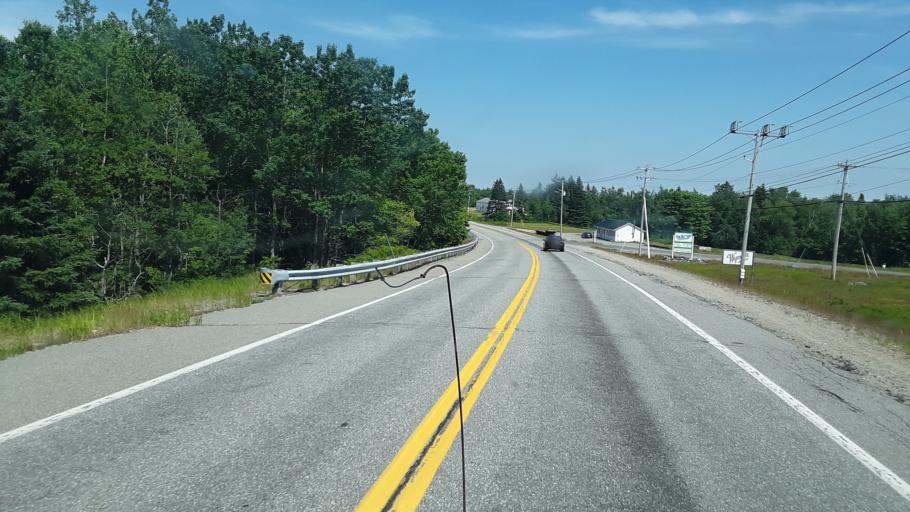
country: US
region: Maine
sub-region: Washington County
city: Jonesport
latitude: 44.6400
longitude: -67.6156
